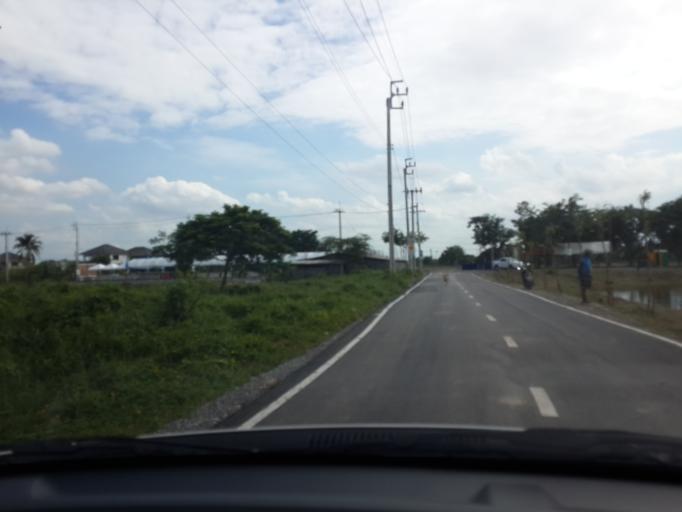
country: TH
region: Bangkok
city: Khlong Sam Wa
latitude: 13.8488
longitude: 100.7763
